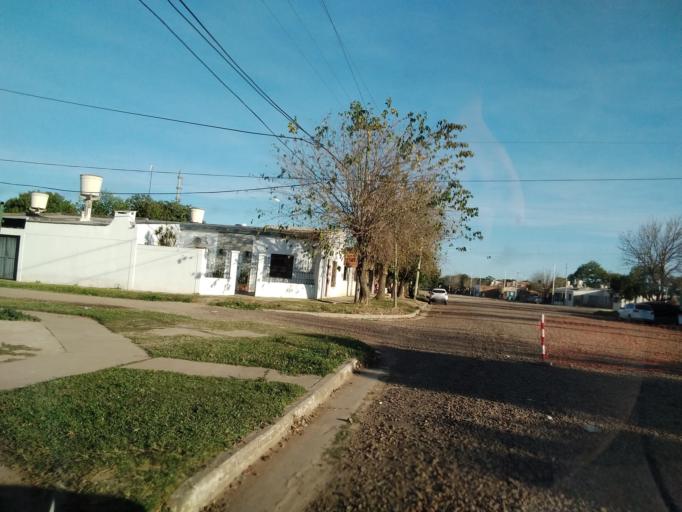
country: AR
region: Corrientes
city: Corrientes
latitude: -27.5050
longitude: -58.8316
